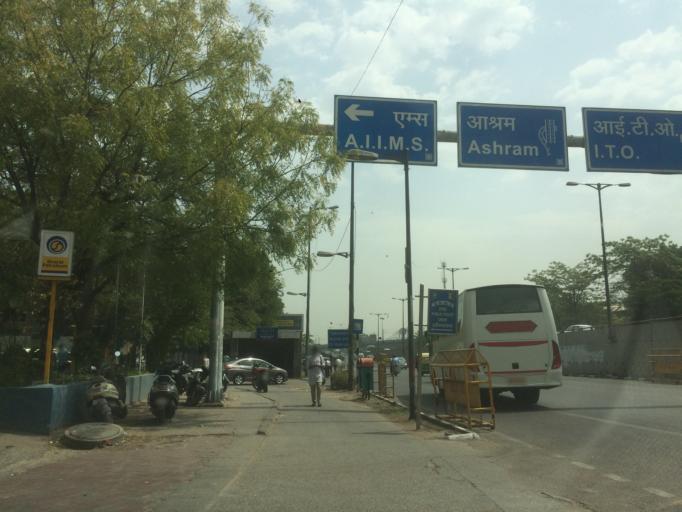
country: IN
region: NCT
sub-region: New Delhi
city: New Delhi
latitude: 28.5628
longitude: 77.2326
